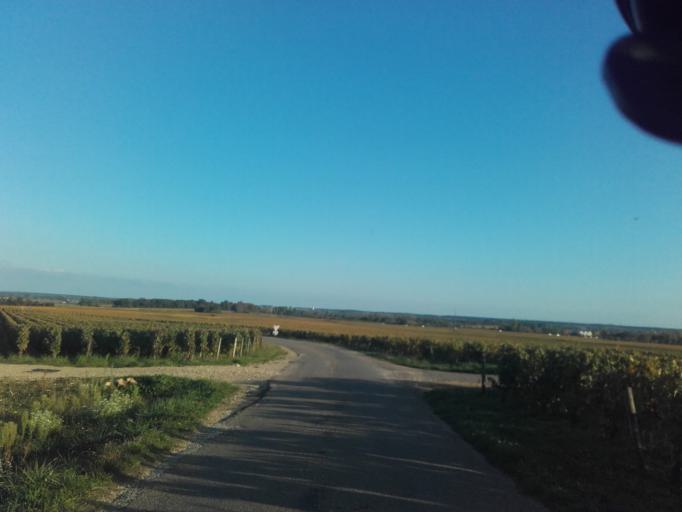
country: FR
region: Bourgogne
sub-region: Departement de la Cote-d'Or
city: Meursault
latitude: 46.9566
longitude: 4.7545
